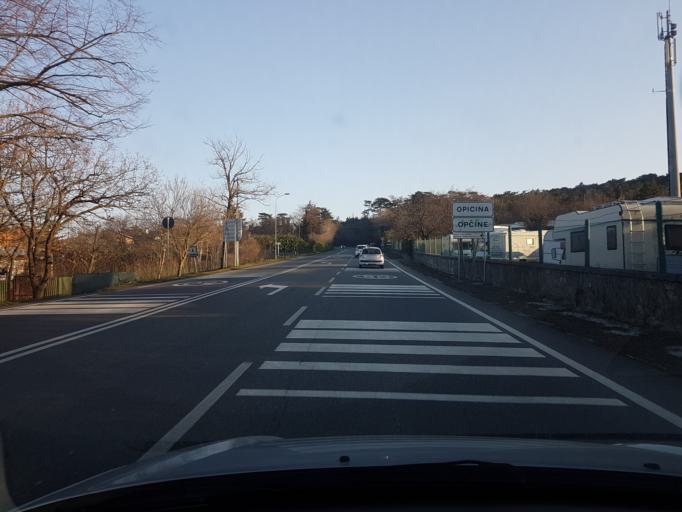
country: IT
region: Friuli Venezia Giulia
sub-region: Provincia di Trieste
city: Villa Opicina
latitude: 45.6895
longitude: 13.7711
